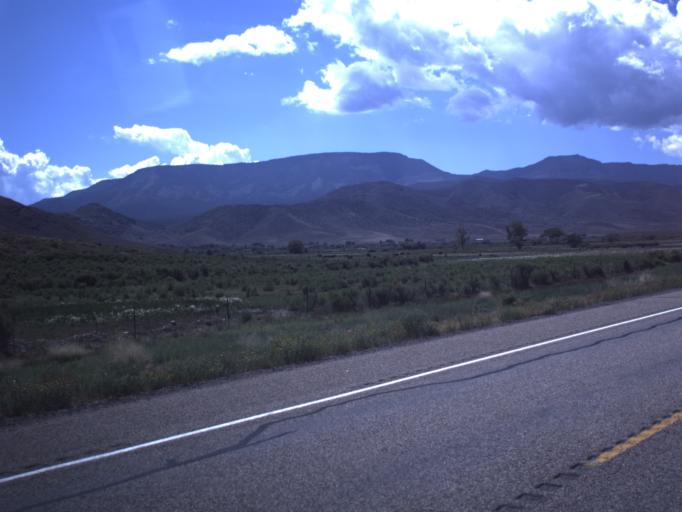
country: US
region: Utah
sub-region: Piute County
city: Junction
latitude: 38.2237
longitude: -112.2198
